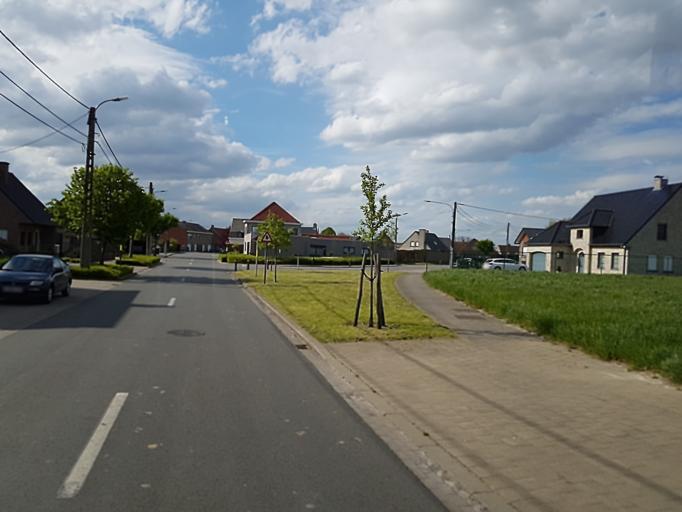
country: BE
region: Flanders
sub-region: Provincie West-Vlaanderen
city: Avelgem
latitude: 50.7814
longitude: 3.4348
